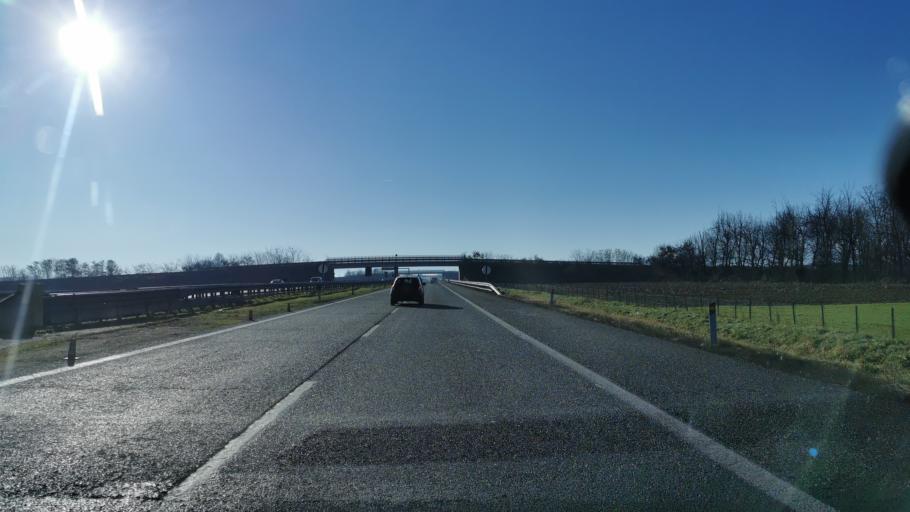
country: IT
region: Piedmont
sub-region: Provincia di Torino
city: Carmagnola
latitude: 44.8405
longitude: 7.7494
